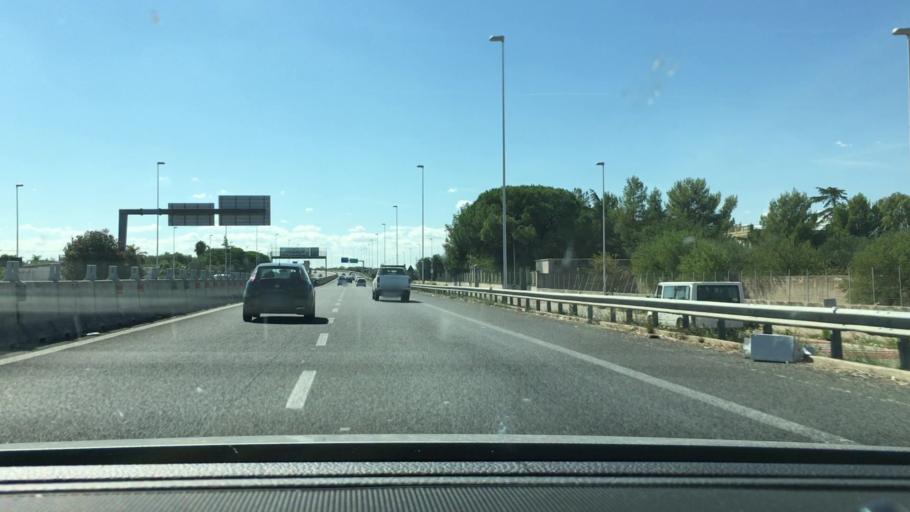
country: IT
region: Apulia
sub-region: Provincia di Bari
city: Bitritto
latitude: 41.0777
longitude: 16.8323
